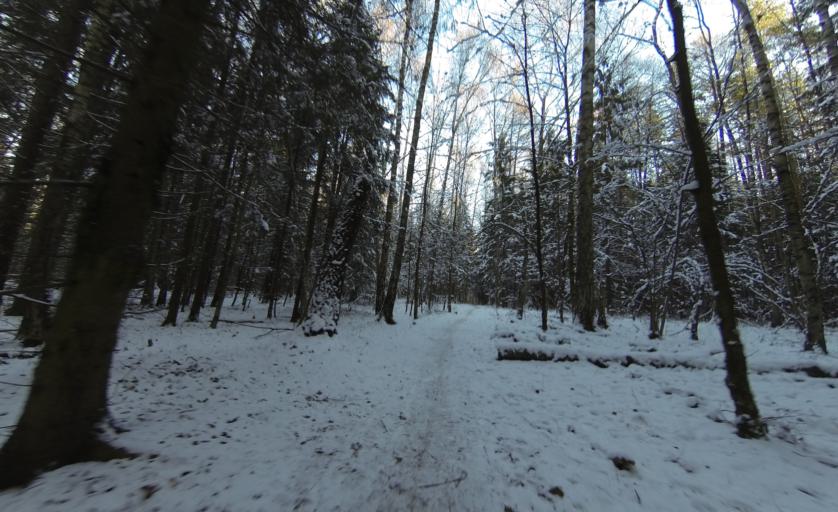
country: RU
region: Moscow
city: Metrogorodok
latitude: 55.8484
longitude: 37.7747
